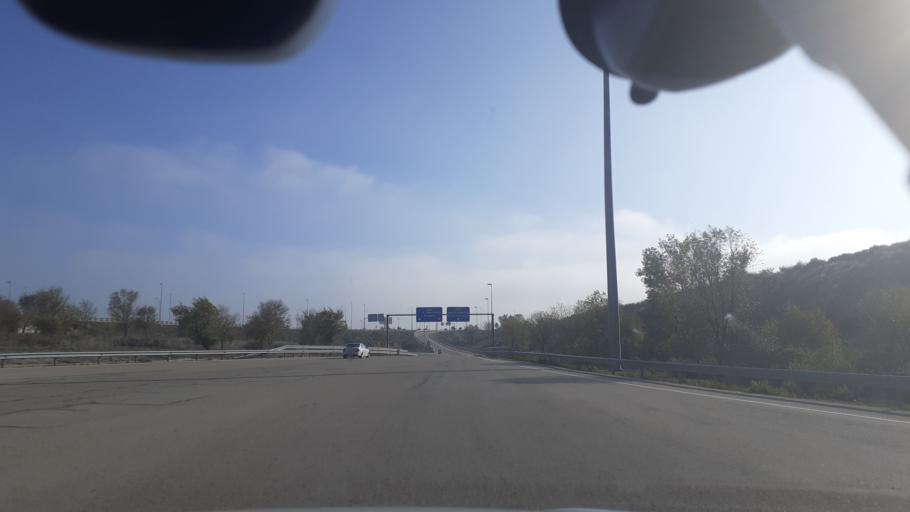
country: ES
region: Madrid
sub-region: Provincia de Madrid
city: Vicalvaro
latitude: 40.4024
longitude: -3.5770
